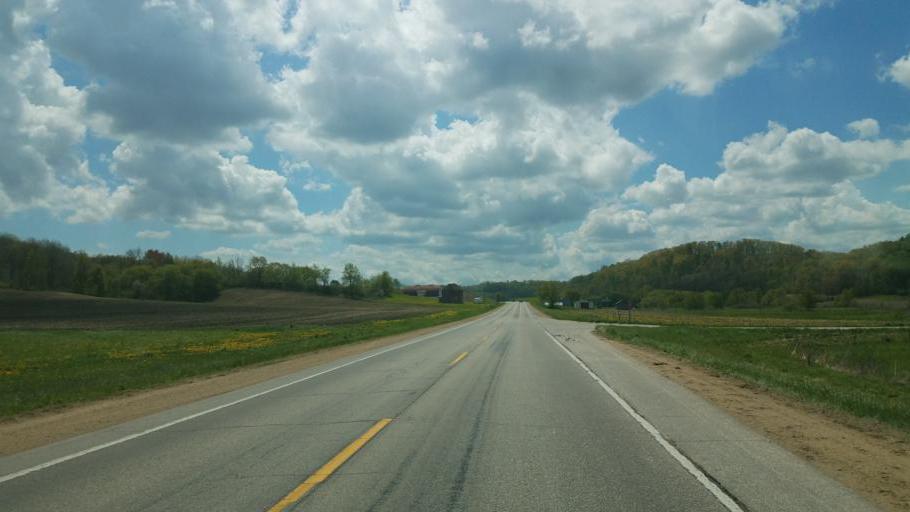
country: US
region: Wisconsin
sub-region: Vernon County
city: Hillsboro
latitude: 43.6270
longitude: -90.3582
